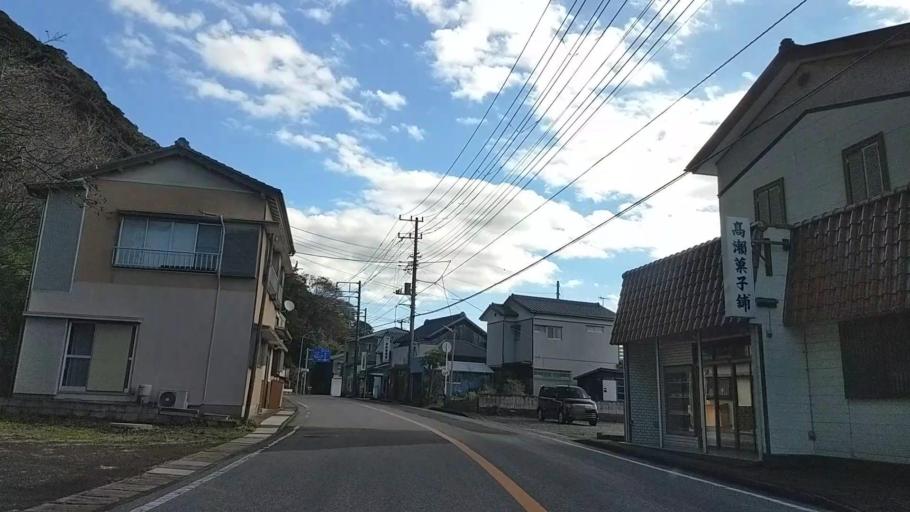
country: JP
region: Chiba
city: Tateyama
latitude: 35.0252
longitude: 139.8576
